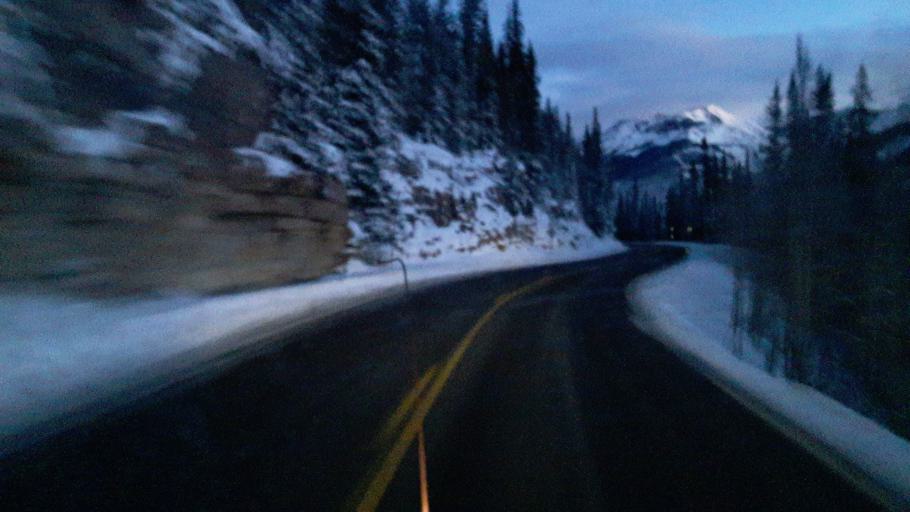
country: US
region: Colorado
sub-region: San Juan County
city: Silverton
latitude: 37.7738
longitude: -107.6708
